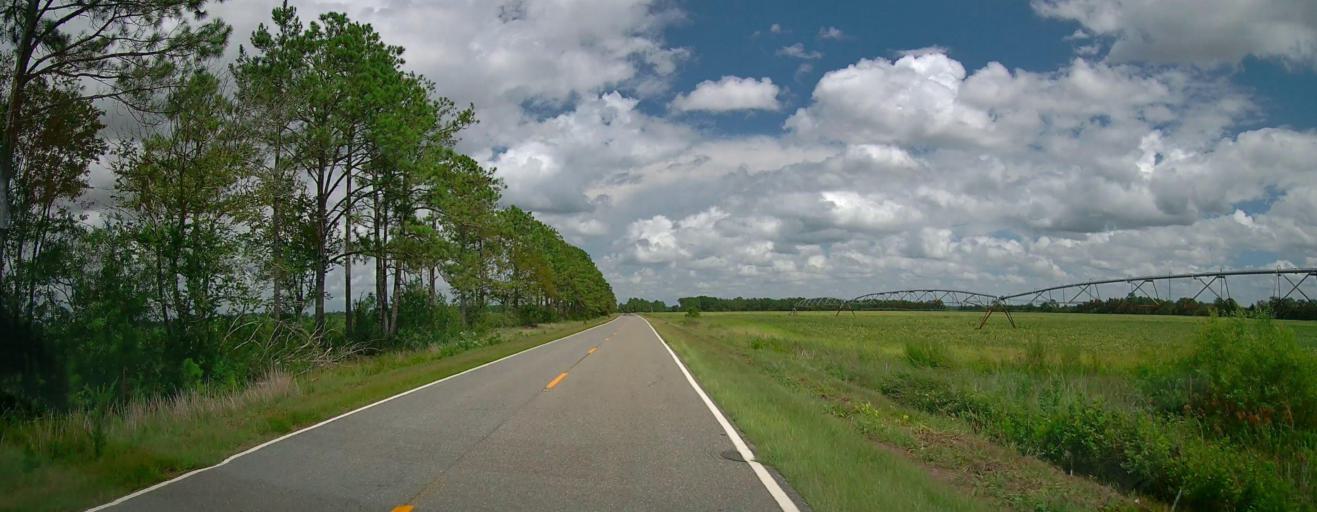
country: US
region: Georgia
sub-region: Irwin County
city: Ocilla
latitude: 31.6459
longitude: -83.3102
